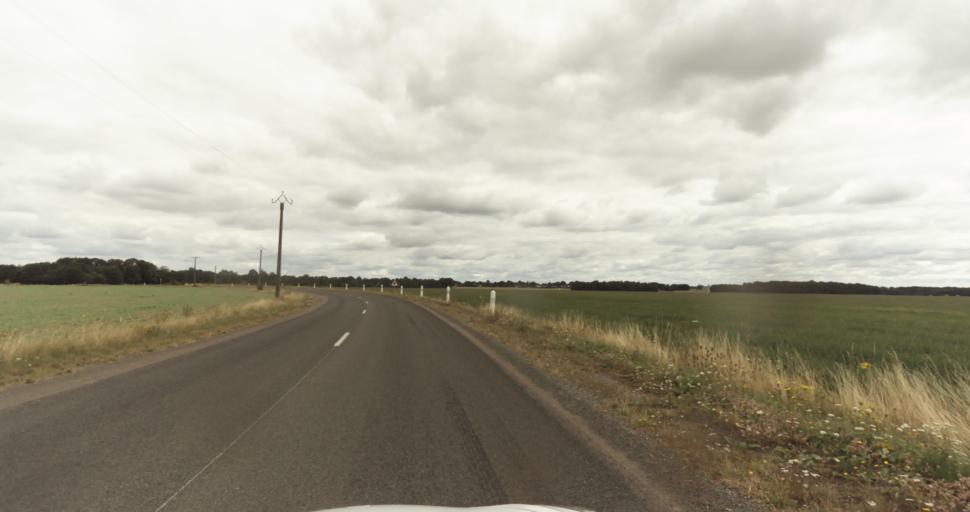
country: FR
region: Haute-Normandie
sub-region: Departement de l'Eure
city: La Madeleine-de-Nonancourt
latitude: 48.8330
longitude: 1.2288
